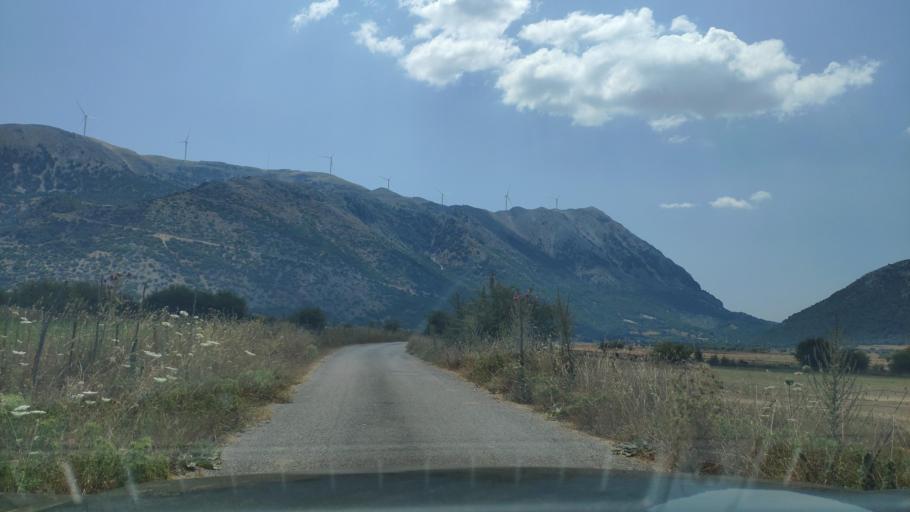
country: GR
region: West Greece
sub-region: Nomos Aitolias kai Akarnanias
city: Monastirakion
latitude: 38.7902
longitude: 20.9622
